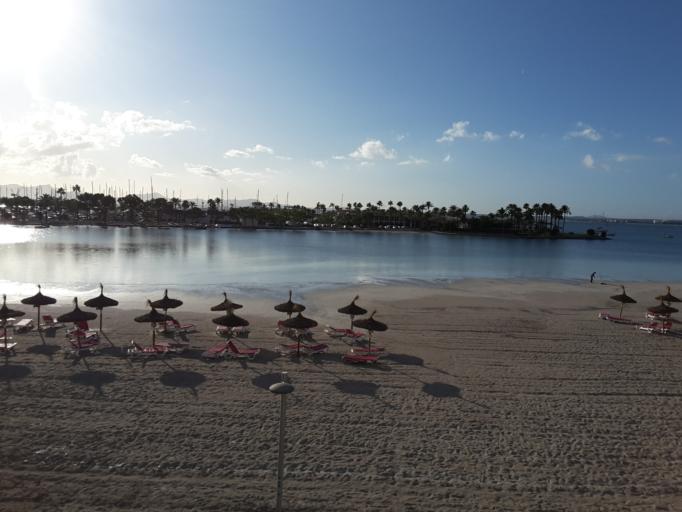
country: ES
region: Balearic Islands
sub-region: Illes Balears
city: Port d'Alcudia
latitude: 39.8413
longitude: 3.1307
